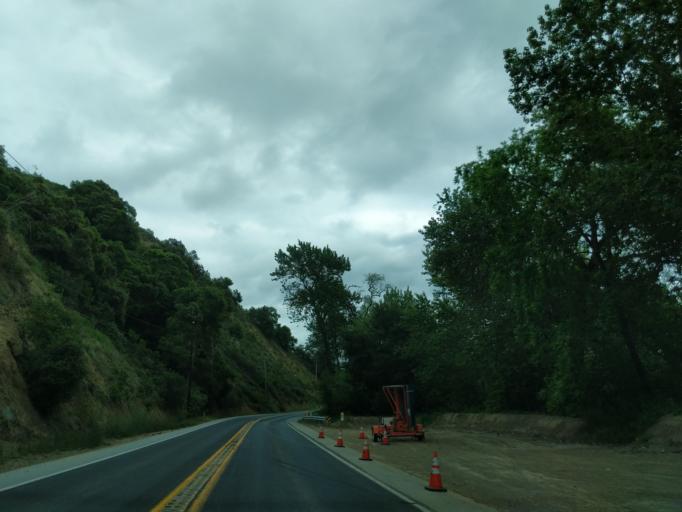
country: US
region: California
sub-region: San Benito County
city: Aromas
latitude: 36.9126
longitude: -121.6532
